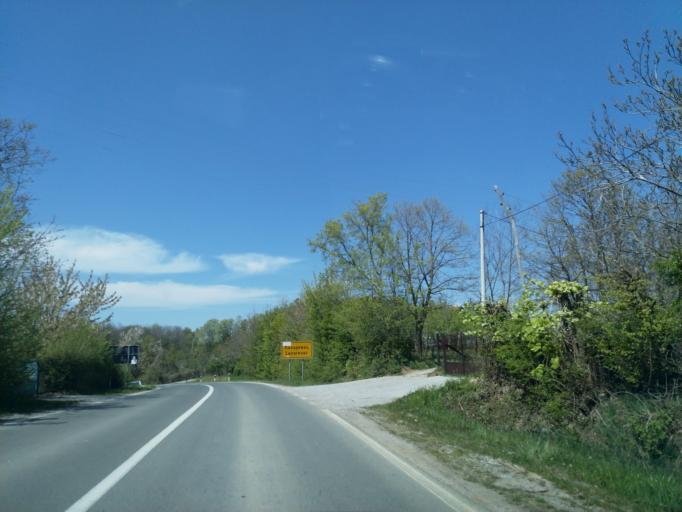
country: RS
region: Central Serbia
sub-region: Belgrade
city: Lazarevac
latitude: 44.3721
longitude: 20.3168
